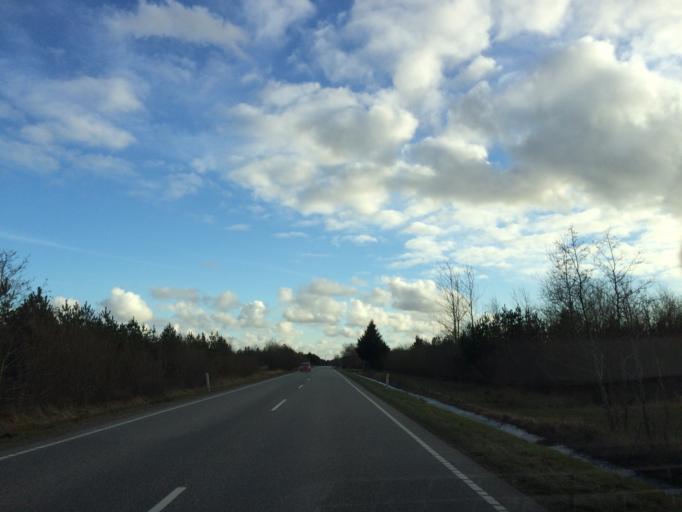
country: DK
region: Central Jutland
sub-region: Holstebro Kommune
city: Ulfborg
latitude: 56.3755
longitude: 8.3301
